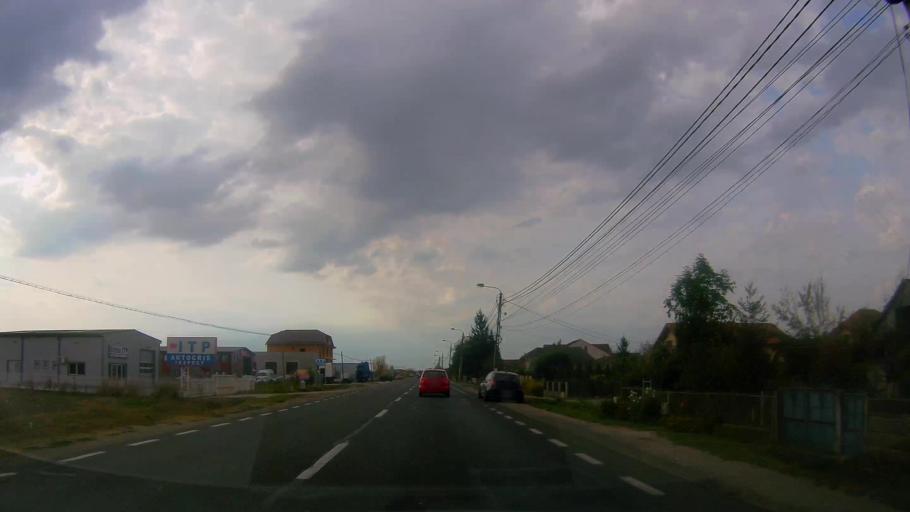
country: RO
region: Satu Mare
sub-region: Comuna Paulesti
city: Paulesti
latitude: 47.7536
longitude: 22.8831
